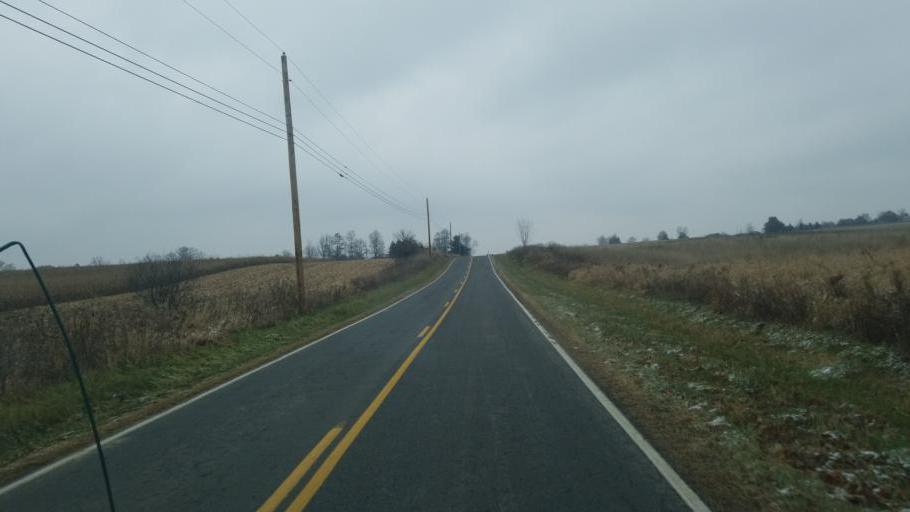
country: US
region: Ohio
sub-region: Medina County
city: Lodi
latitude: 41.1303
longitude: -82.0020
